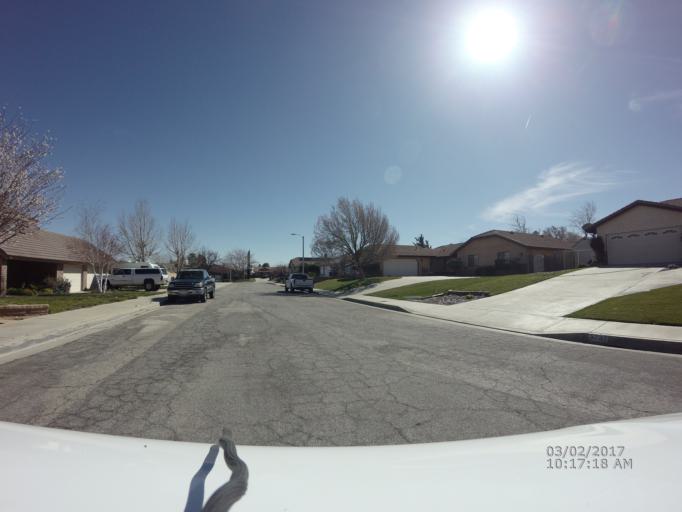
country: US
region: California
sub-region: Los Angeles County
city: Quartz Hill
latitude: 34.6413
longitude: -118.2333
